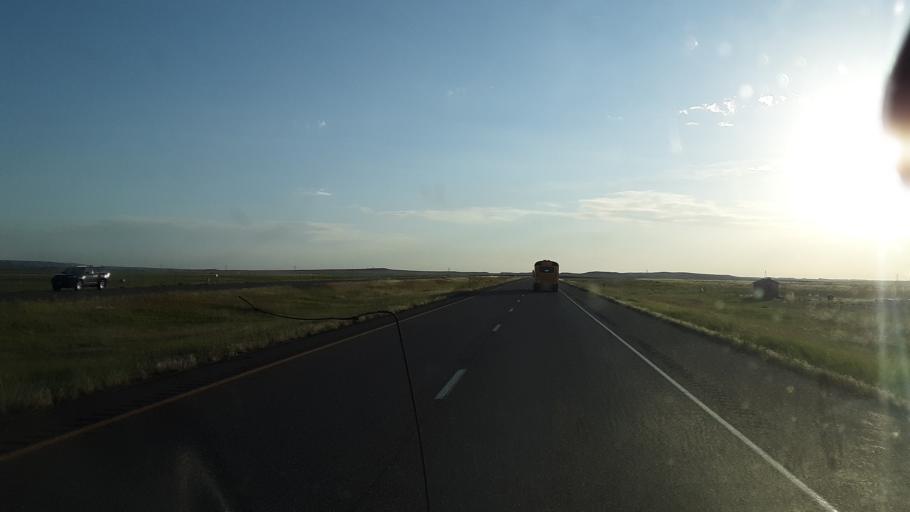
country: US
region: Montana
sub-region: Big Horn County
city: Hardin
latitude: 45.7464
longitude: -107.6608
